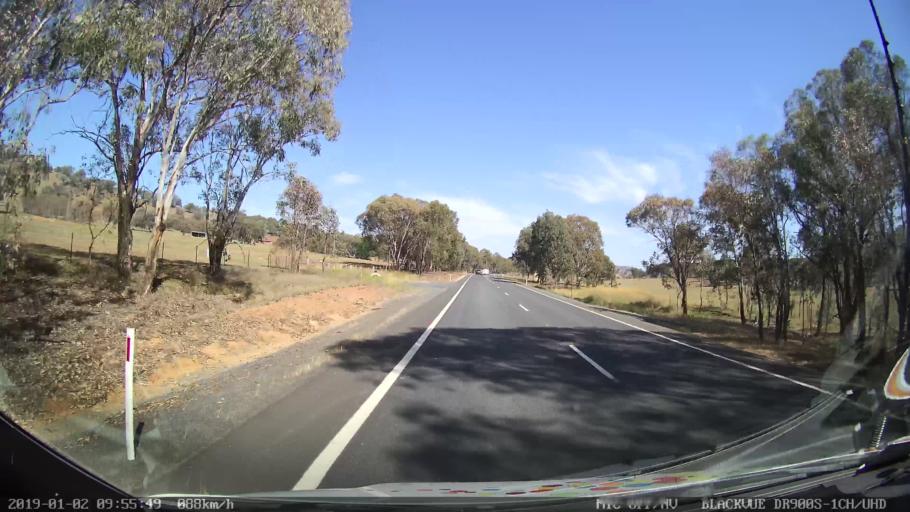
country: AU
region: New South Wales
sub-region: Tumut Shire
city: Tumut
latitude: -35.2207
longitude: 148.1835
